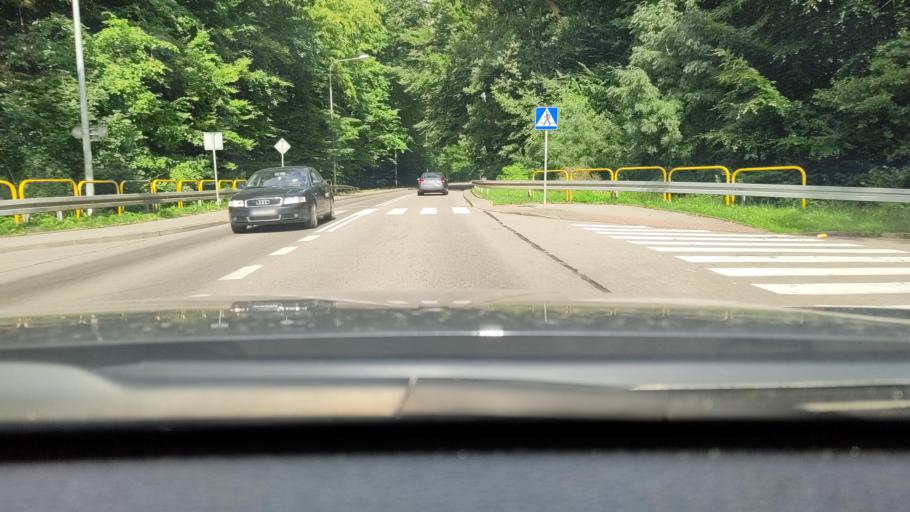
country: PL
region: Pomeranian Voivodeship
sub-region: Powiat wejherowski
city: Wejherowo
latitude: 54.5923
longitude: 18.2382
